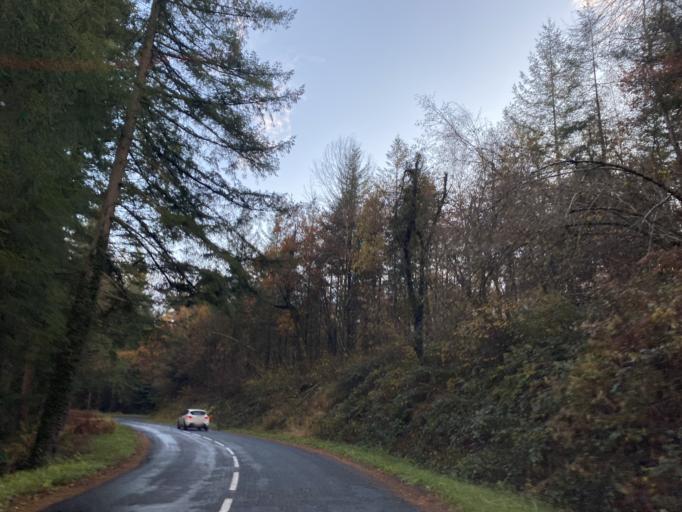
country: FR
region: Auvergne
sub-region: Departement du Puy-de-Dome
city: Courpiere
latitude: 45.7056
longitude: 3.6072
